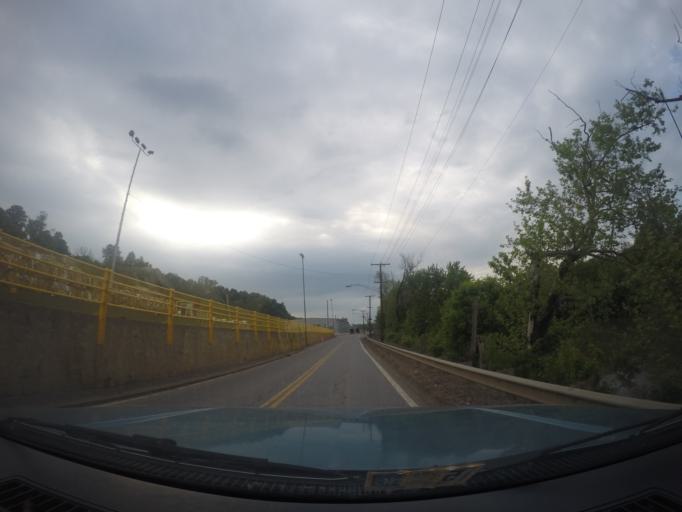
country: US
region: Virginia
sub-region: City of Lynchburg
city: Lynchburg
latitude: 37.4025
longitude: -79.1267
